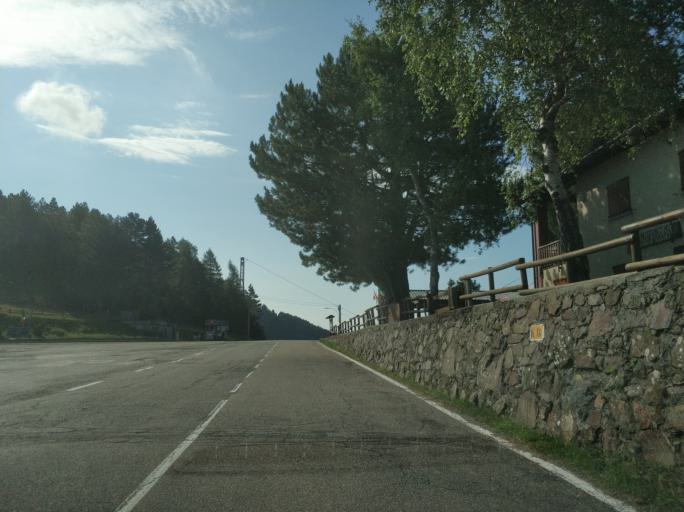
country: IT
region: Piedmont
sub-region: Provincia di Torino
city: Rubiana
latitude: 45.1783
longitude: 7.3821
